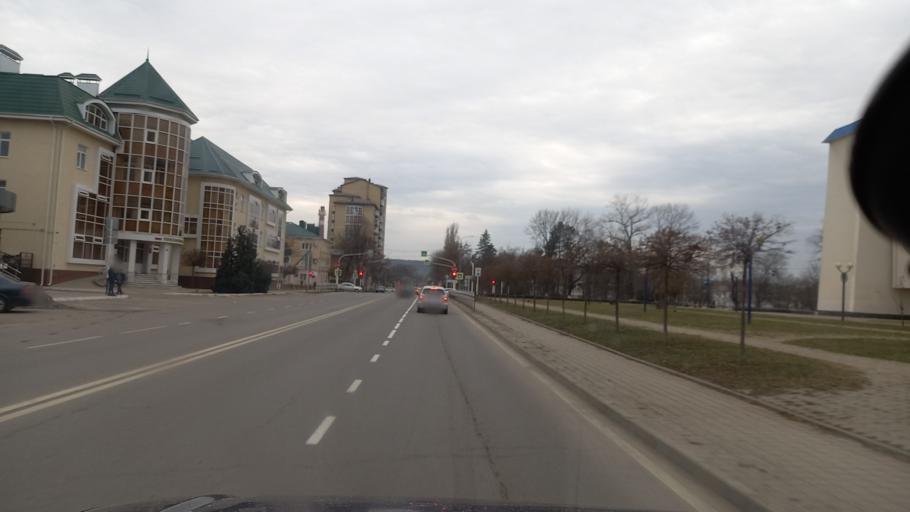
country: RU
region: Adygeya
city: Maykop
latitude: 44.6092
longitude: 40.1003
